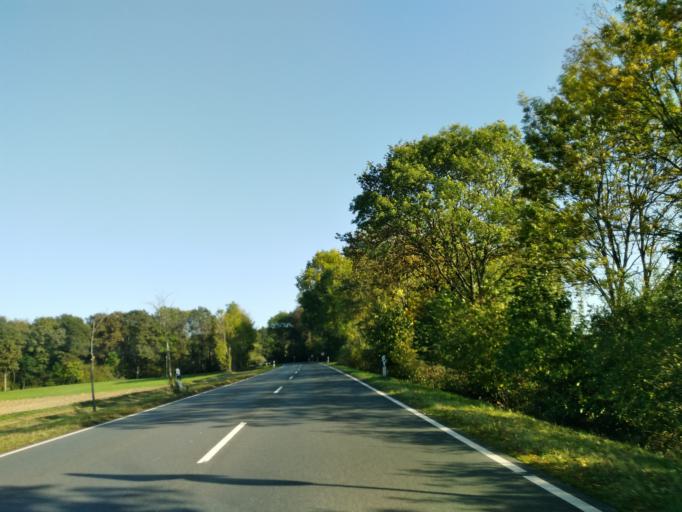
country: DE
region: Rheinland-Pfalz
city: Kircheib
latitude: 50.7075
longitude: 7.4282
